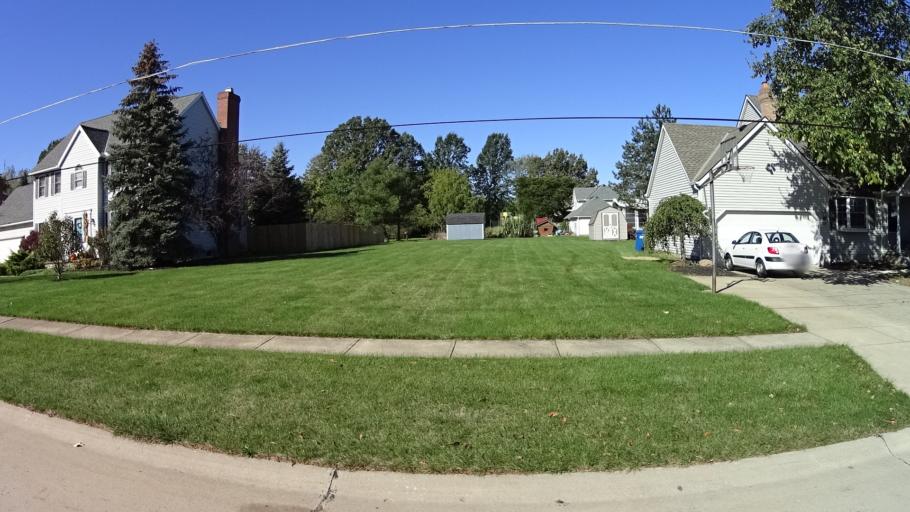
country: US
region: Ohio
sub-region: Lorain County
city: Amherst
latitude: 41.4028
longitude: -82.2451
